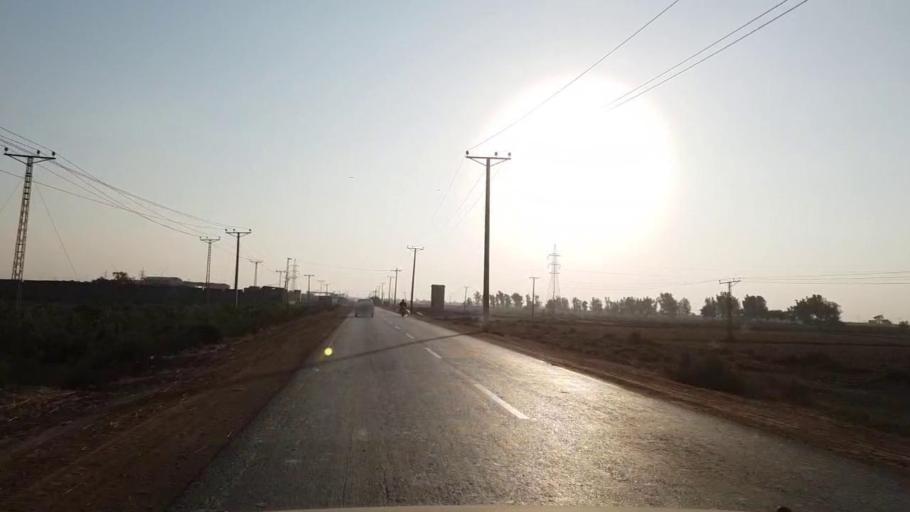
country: PK
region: Sindh
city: Daro Mehar
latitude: 24.6190
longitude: 68.0938
